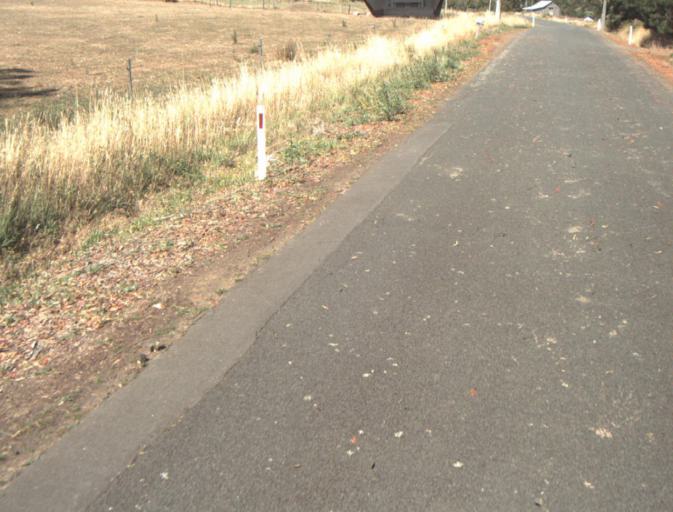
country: AU
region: Tasmania
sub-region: Launceston
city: Newstead
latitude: -41.3379
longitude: 147.3039
